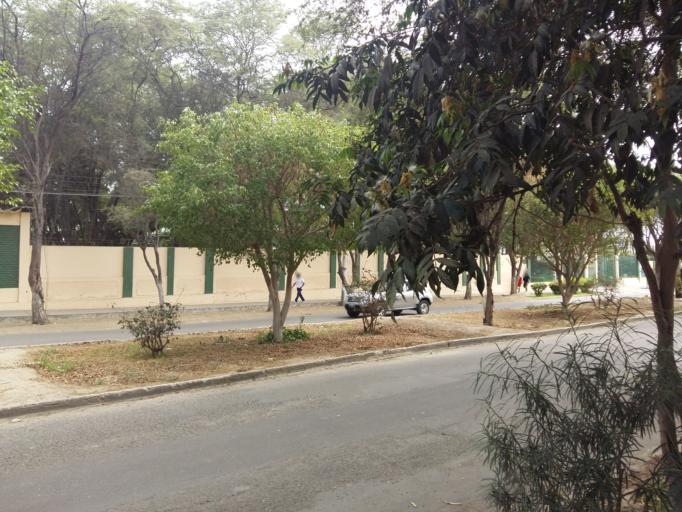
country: PE
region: Piura
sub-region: Provincia de Piura
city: Piura
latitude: -5.1884
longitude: -80.6198
